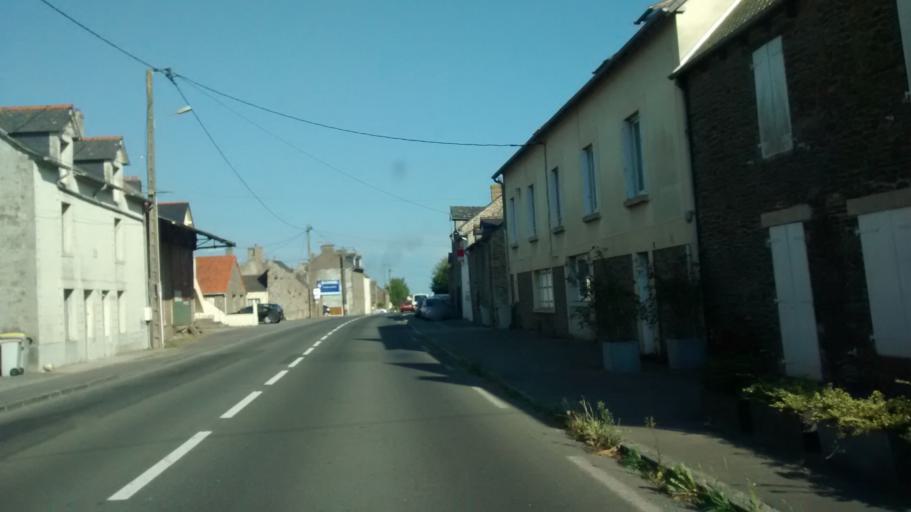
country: FR
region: Brittany
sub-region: Departement d'Ille-et-Vilaine
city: Saint-Meloir-des-Ondes
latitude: 48.6453
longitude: -1.8909
